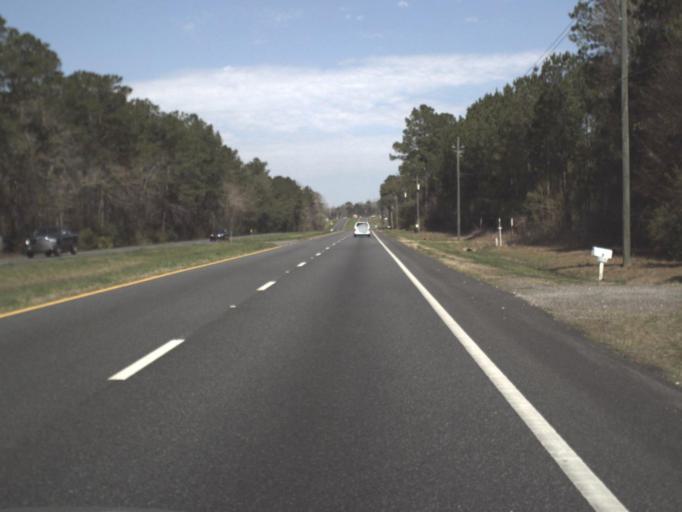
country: US
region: Florida
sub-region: Gadsden County
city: Havana
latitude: 30.5793
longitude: -84.3987
